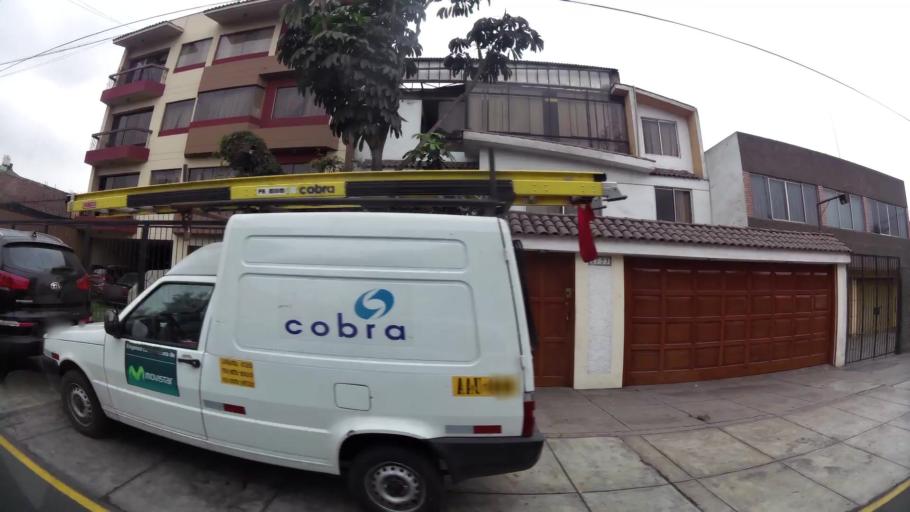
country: PE
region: Lima
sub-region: Lima
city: San Luis
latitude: -12.1027
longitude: -76.9942
